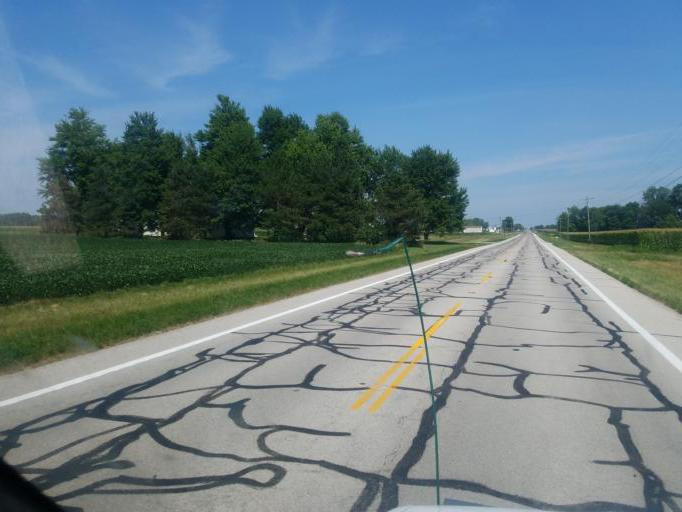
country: US
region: Ohio
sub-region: Auglaize County
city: Saint Marys
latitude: 40.4947
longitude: -84.4784
